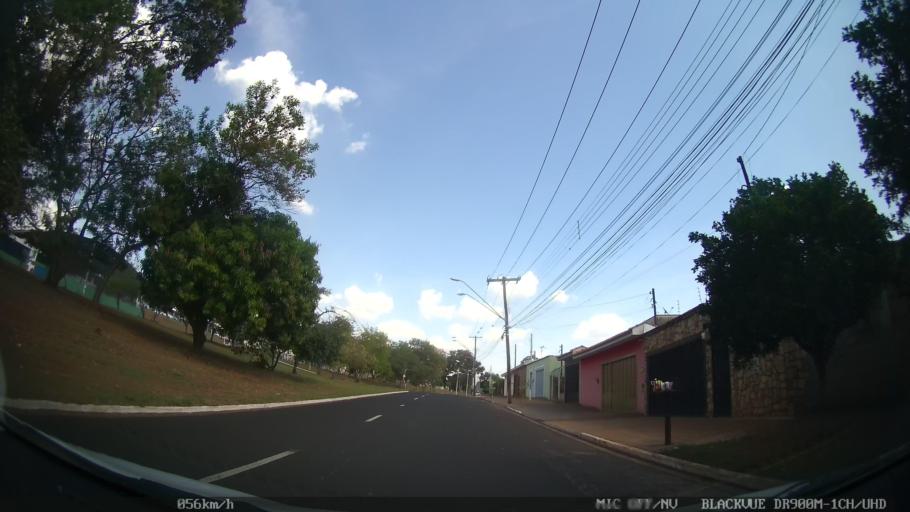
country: BR
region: Sao Paulo
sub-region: Ribeirao Preto
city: Ribeirao Preto
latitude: -21.1826
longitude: -47.8414
